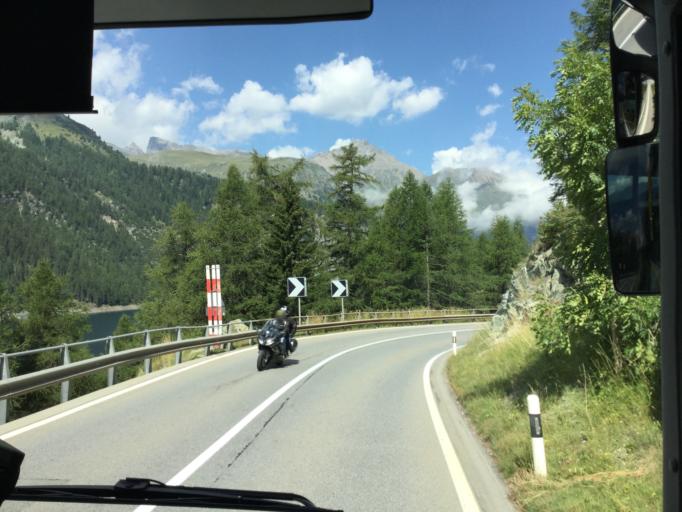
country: CH
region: Grisons
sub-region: Maloja District
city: Silvaplana
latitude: 46.4972
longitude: 9.6422
